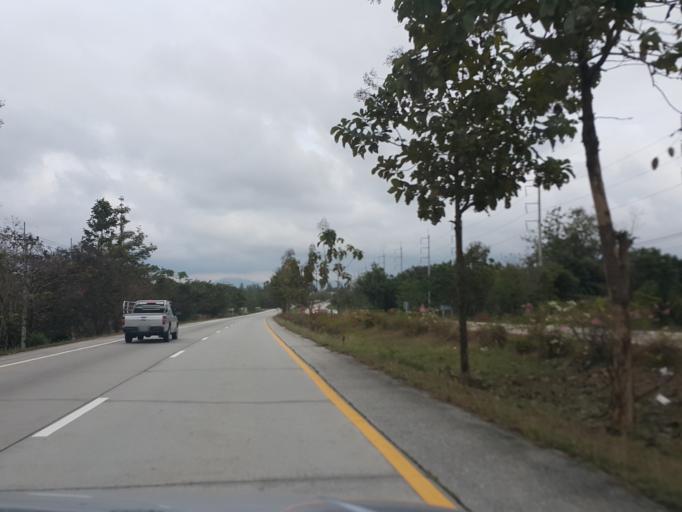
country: TH
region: Lampang
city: Hang Chat
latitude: 18.3156
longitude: 99.3760
